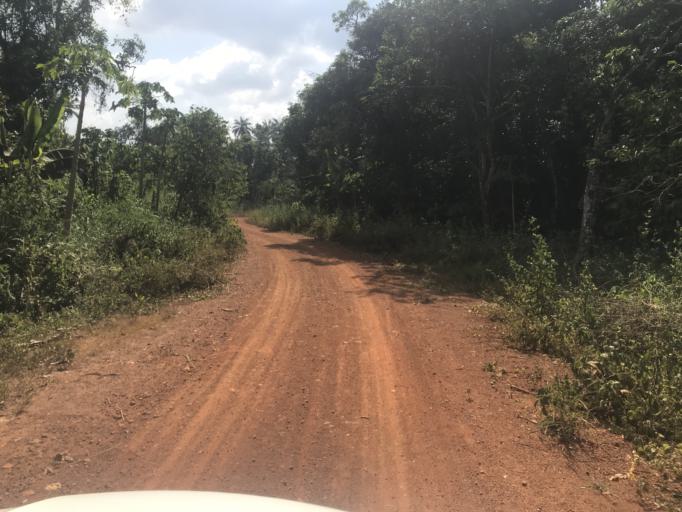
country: NG
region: Osun
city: Ibokun
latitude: 7.8124
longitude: 4.6960
